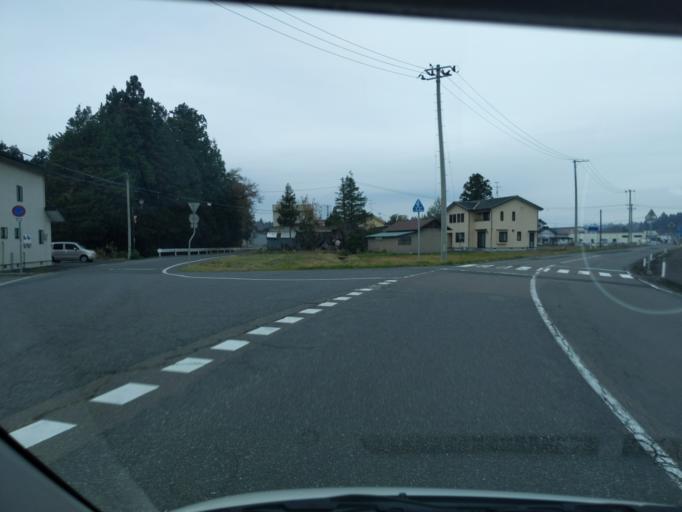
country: JP
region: Iwate
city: Mizusawa
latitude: 39.0989
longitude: 141.0838
